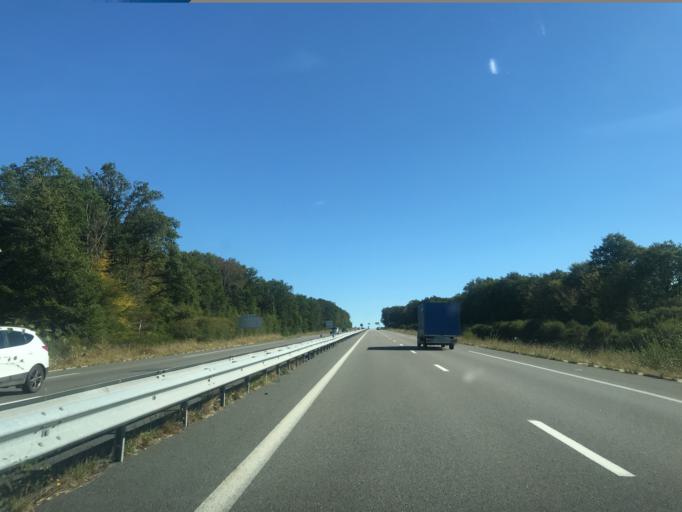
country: FR
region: Limousin
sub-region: Departement de la Creuse
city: Chambon-sur-Voueize
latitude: 46.2509
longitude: 2.3533
